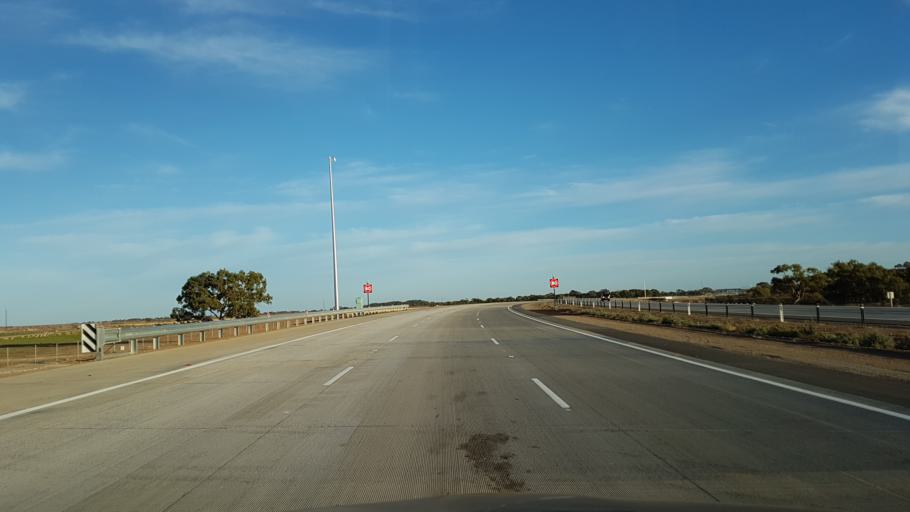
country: AU
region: South Australia
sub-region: Salisbury
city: Salisbury
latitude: -34.7521
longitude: 138.5829
